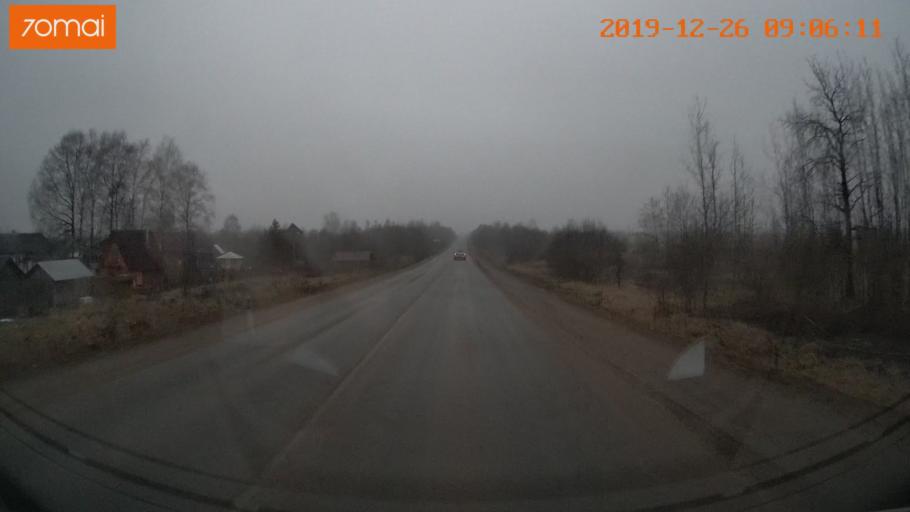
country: RU
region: Vologda
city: Gryazovets
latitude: 58.8333
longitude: 40.2545
